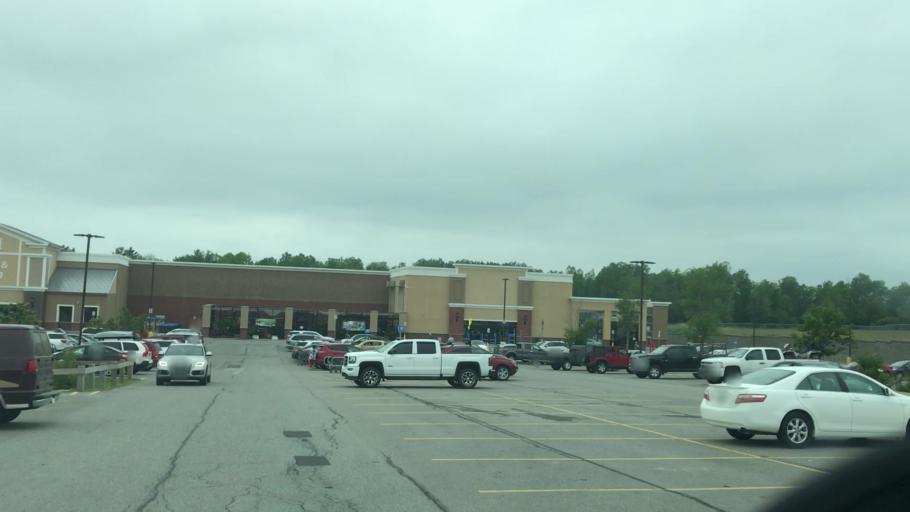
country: US
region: Maine
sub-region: Penobscot County
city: Veazie
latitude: 44.8408
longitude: -68.7475
